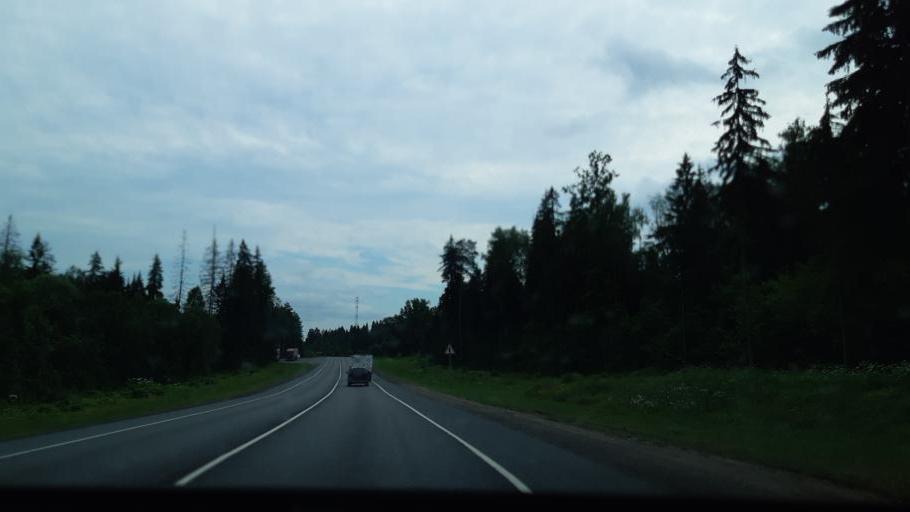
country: RU
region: Moskovskaya
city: Dorokhovo
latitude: 55.4843
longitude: 36.3565
